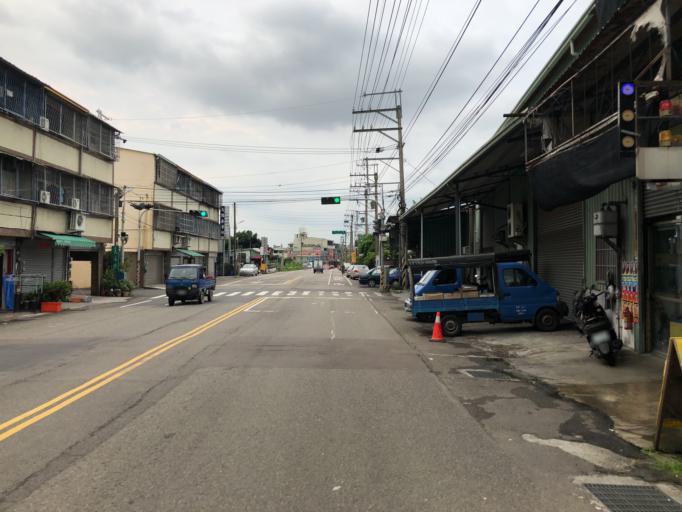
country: TW
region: Taiwan
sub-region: Taichung City
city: Taichung
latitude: 24.0937
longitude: 120.7292
